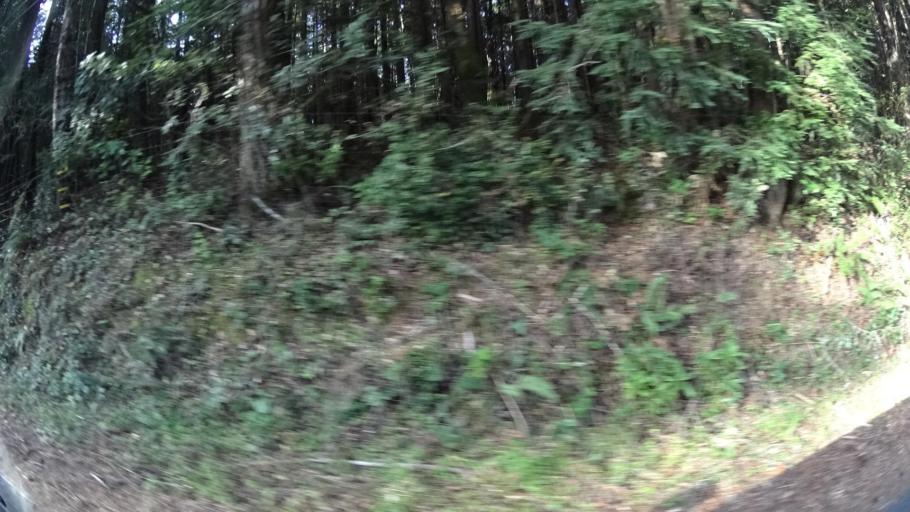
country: US
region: California
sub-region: Humboldt County
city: Bayside
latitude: 40.7564
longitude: -123.9891
